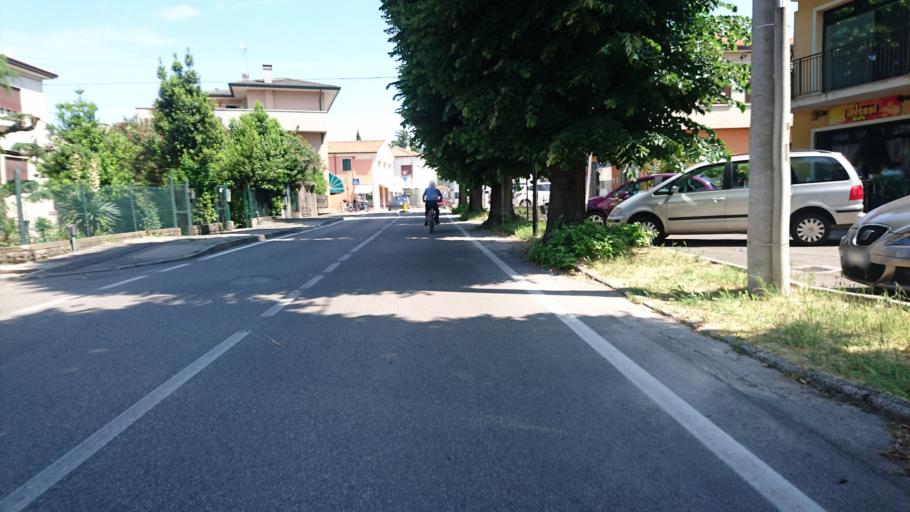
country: IT
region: Veneto
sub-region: Provincia di Padova
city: Este
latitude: 45.2251
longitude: 11.6460
